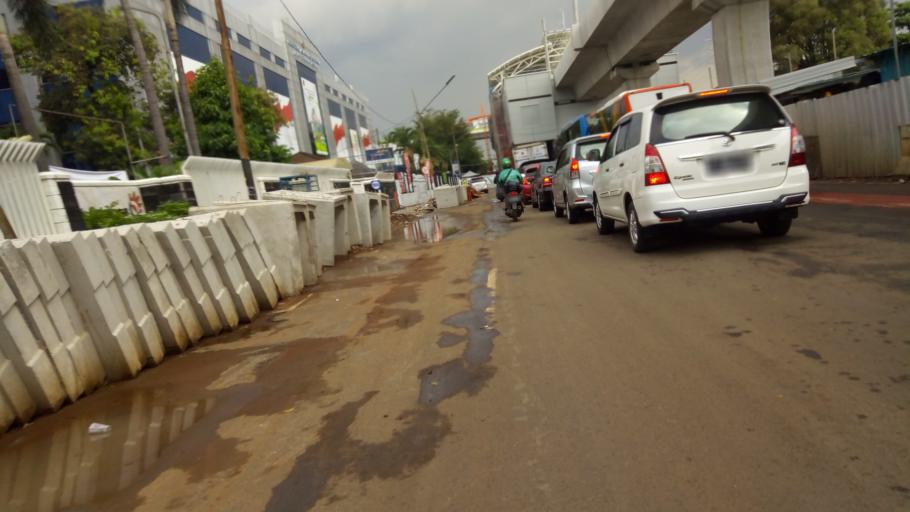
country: ID
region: Jakarta Raya
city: Jakarta
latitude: -6.2371
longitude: 106.7986
